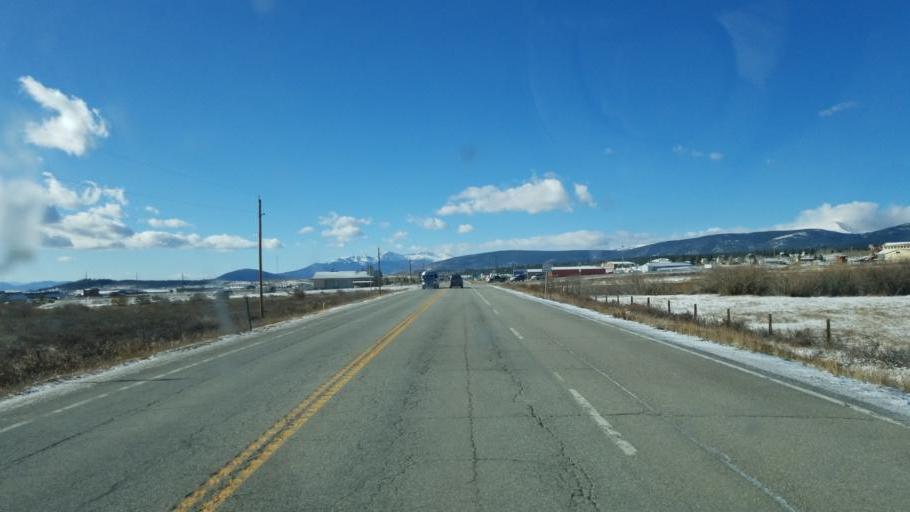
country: US
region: Colorado
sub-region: Park County
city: Fairplay
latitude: 39.2305
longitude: -105.9877
